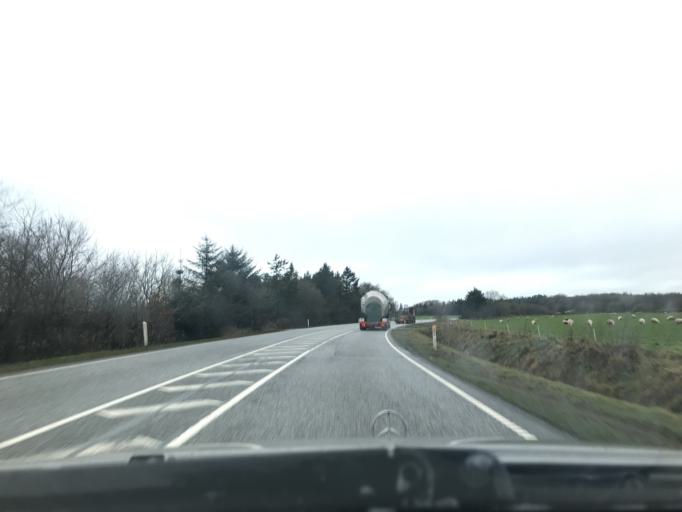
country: DK
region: South Denmark
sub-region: Haderslev Kommune
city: Gram
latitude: 55.2337
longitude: 8.9425
